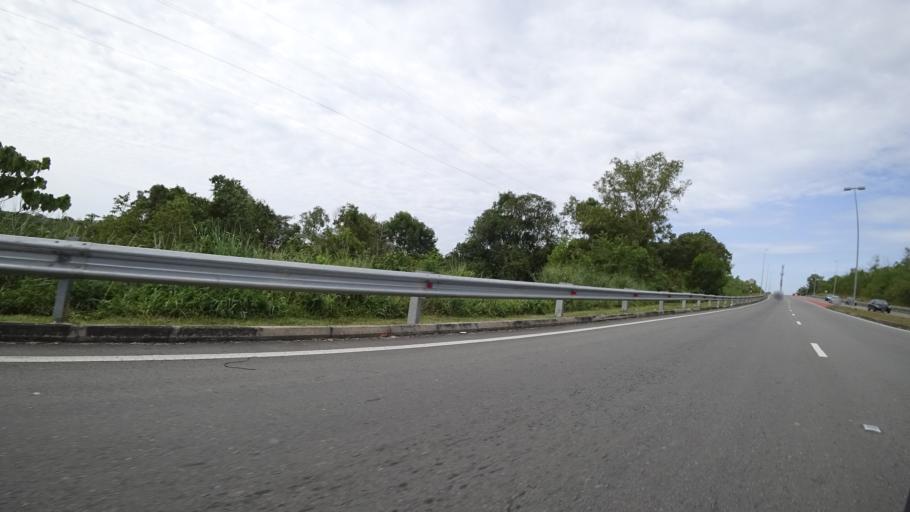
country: BN
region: Brunei and Muara
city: Bandar Seri Begawan
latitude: 4.9329
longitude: 114.8852
